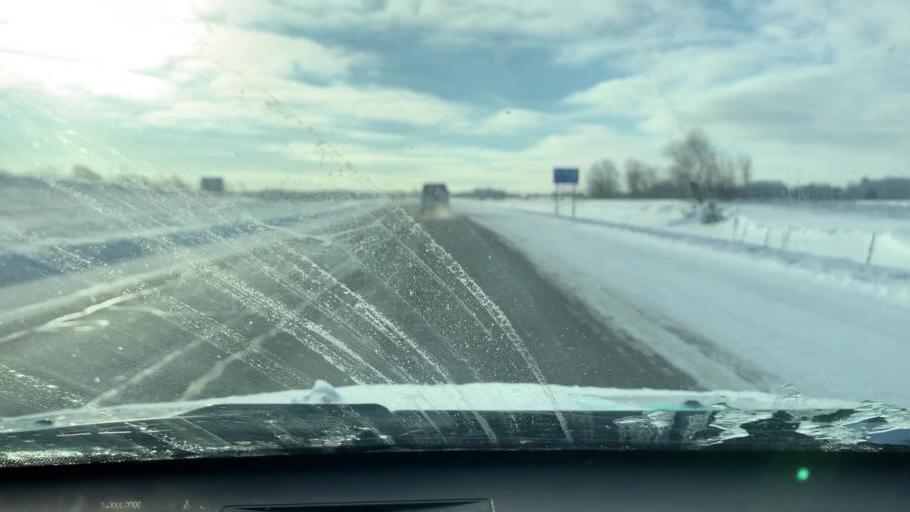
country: US
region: Michigan
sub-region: Wexford County
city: Cadillac
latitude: 44.2605
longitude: -85.3829
